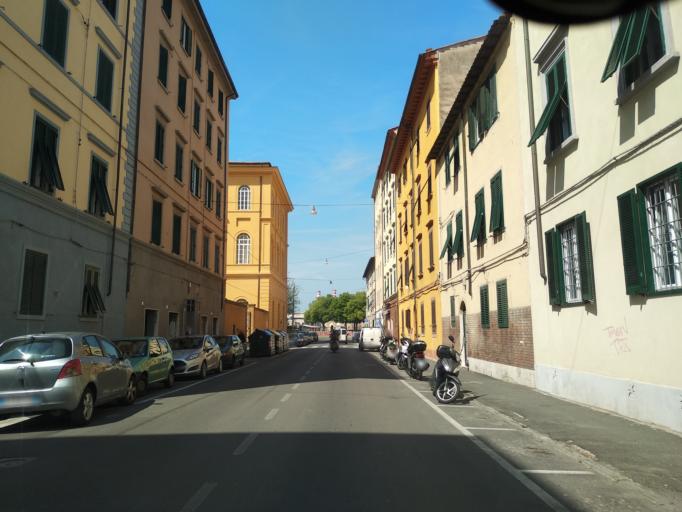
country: IT
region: Tuscany
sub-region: Provincia di Livorno
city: Livorno
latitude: 43.5585
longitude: 10.3158
